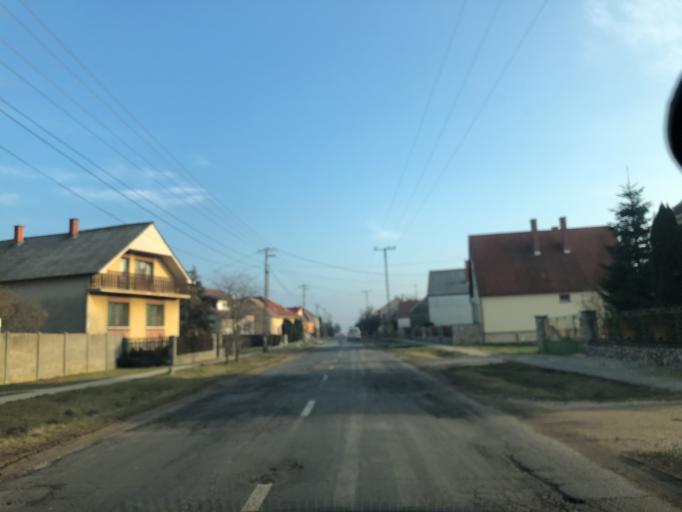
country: HU
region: Gyor-Moson-Sopron
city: Kapuvar
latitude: 47.5931
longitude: 17.0930
